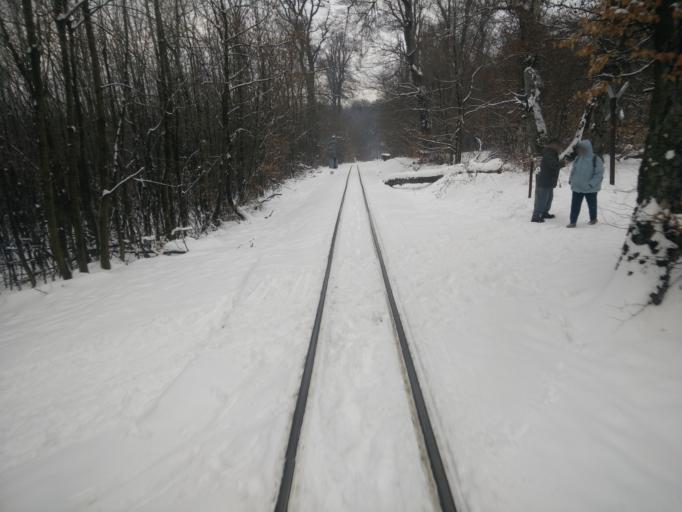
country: HU
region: Pest
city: Budakeszi
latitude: 47.5013
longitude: 18.9601
